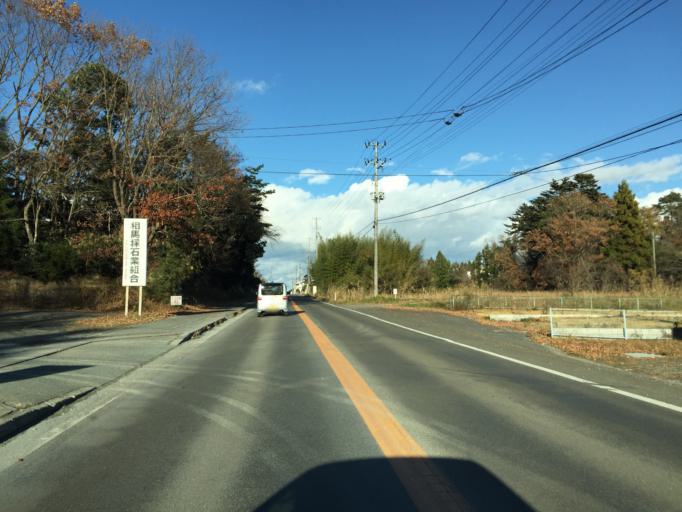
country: JP
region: Miyagi
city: Marumori
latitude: 37.8117
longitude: 140.9392
